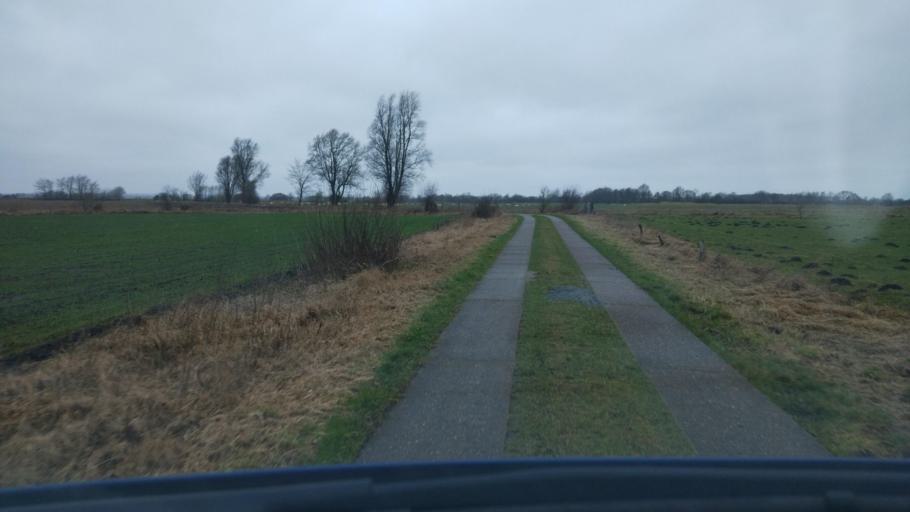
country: DE
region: Schleswig-Holstein
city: Gross Rheide
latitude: 54.4586
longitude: 9.4190
